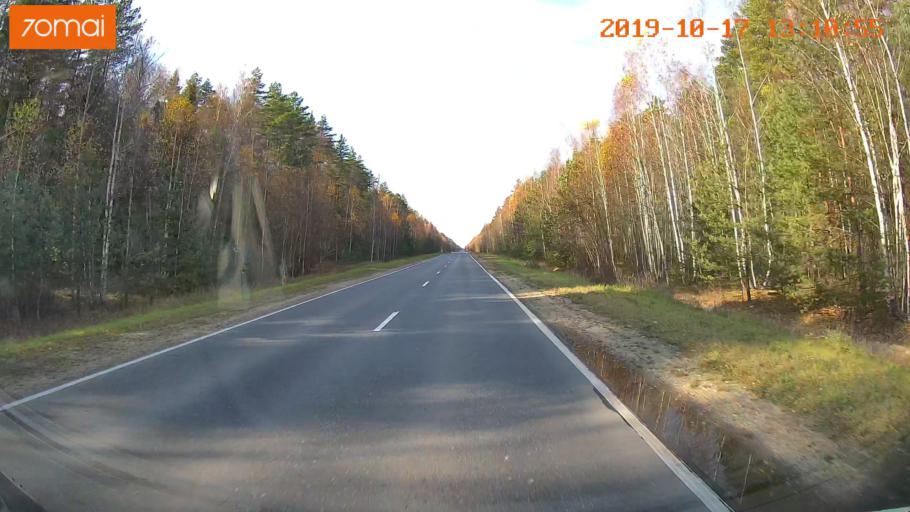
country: RU
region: Rjazan
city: Syntul
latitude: 55.0232
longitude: 41.2468
